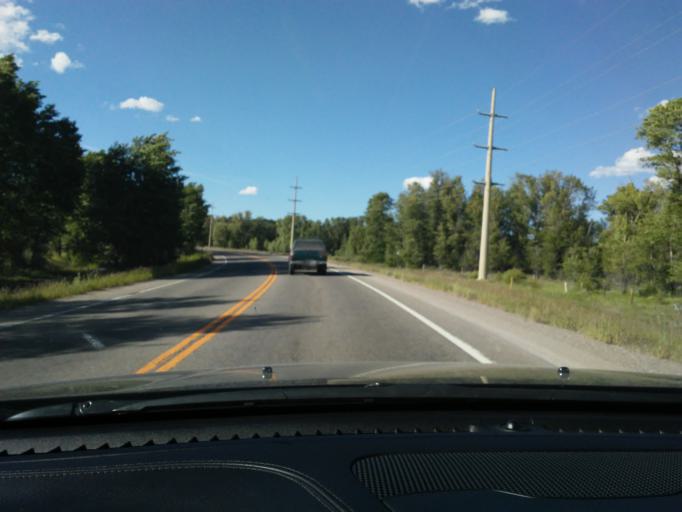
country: US
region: Wyoming
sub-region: Teton County
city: Moose Wilson Road
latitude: 43.5406
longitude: -110.8226
